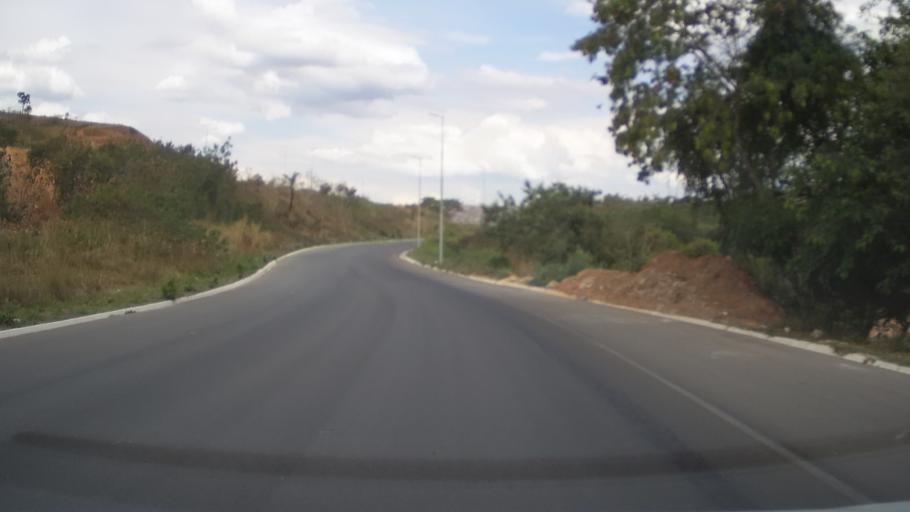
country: BR
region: Minas Gerais
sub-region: Belo Horizonte
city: Belo Horizonte
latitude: -19.8710
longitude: -43.8887
